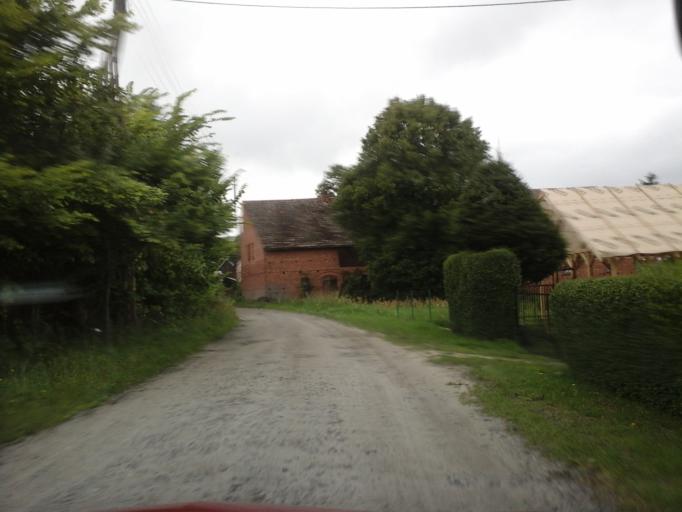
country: PL
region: Lubusz
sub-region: Powiat strzelecko-drezdenecki
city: Dobiegniew
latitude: 53.0776
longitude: 15.7871
